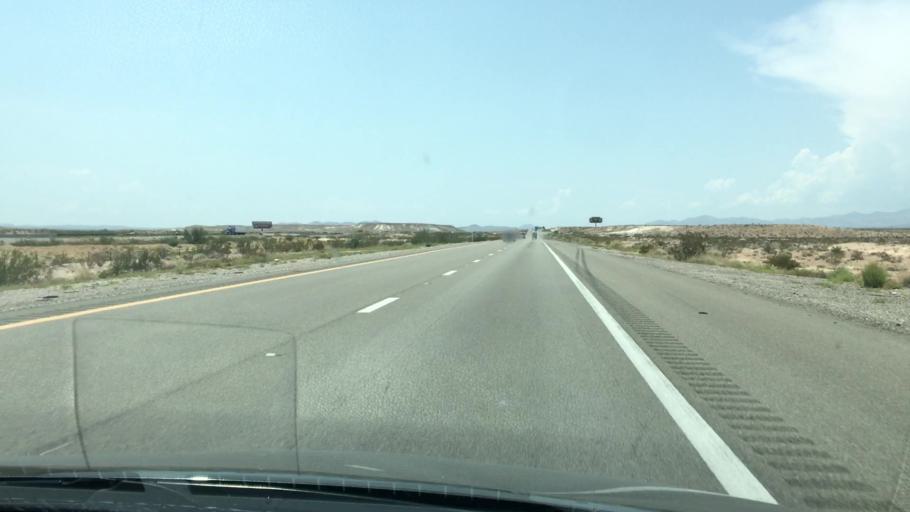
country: US
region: Nevada
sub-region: Clark County
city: Moapa Town
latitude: 36.5589
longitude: -114.6887
